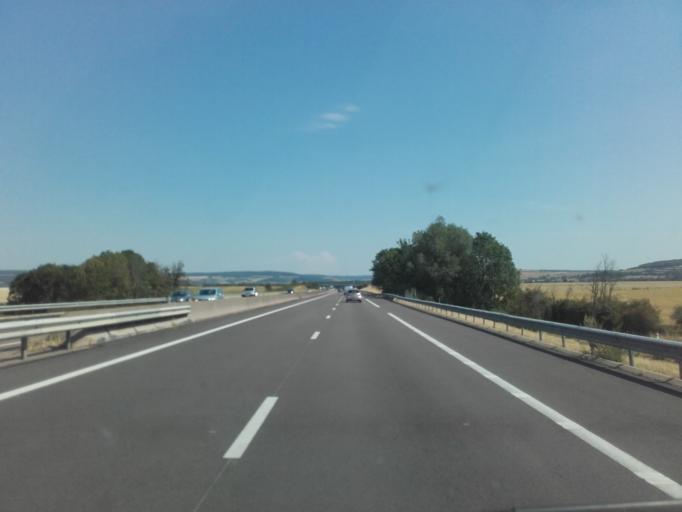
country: FR
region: Bourgogne
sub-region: Departement de la Cote-d'Or
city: Vitteaux
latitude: 47.3631
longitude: 4.4188
